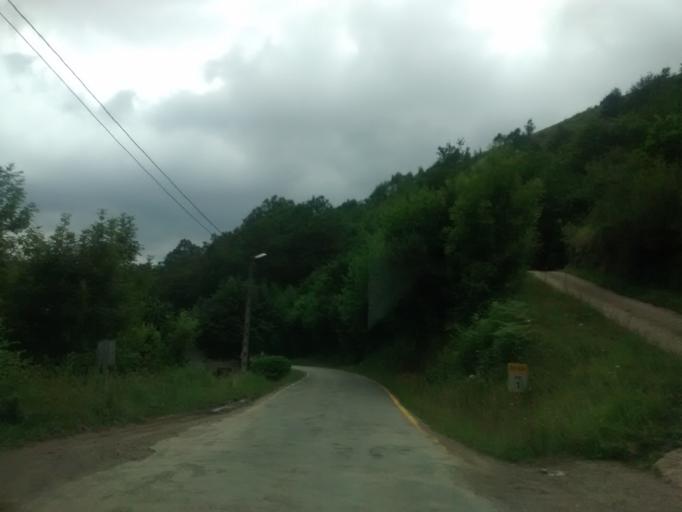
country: ES
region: Cantabria
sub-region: Provincia de Cantabria
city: Vega de Pas
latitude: 43.1497
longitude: -3.7743
